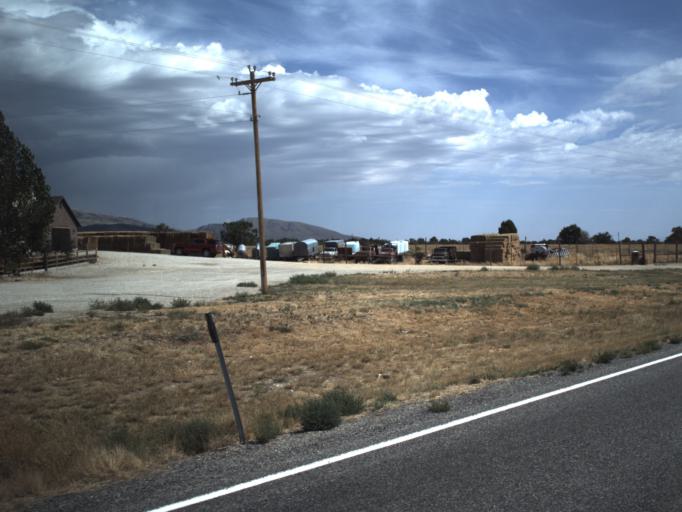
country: US
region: Idaho
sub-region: Cassia County
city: Burley
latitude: 41.8197
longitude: -113.4219
